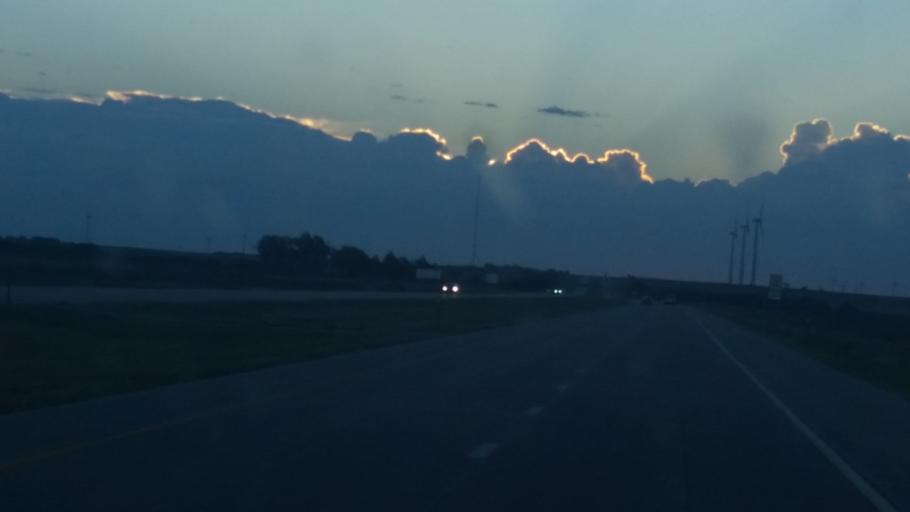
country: US
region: Kansas
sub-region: Ellsworth County
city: Ellsworth
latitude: 38.8485
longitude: -98.3869
